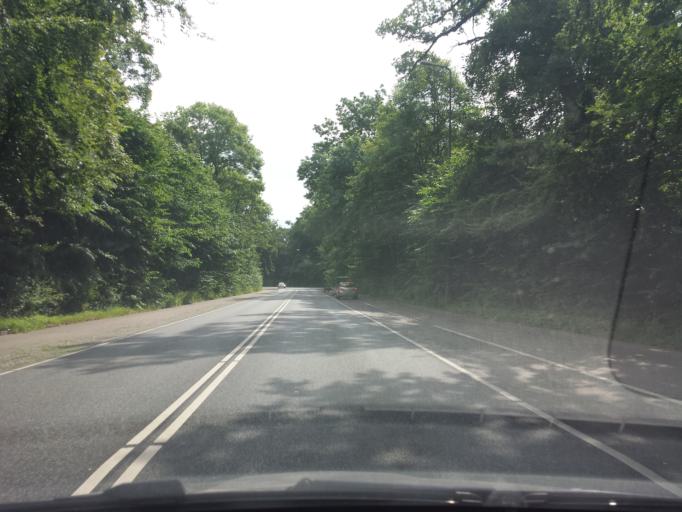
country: DK
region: Capital Region
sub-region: Gentofte Kommune
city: Charlottenlund
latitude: 55.7721
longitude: 12.5507
